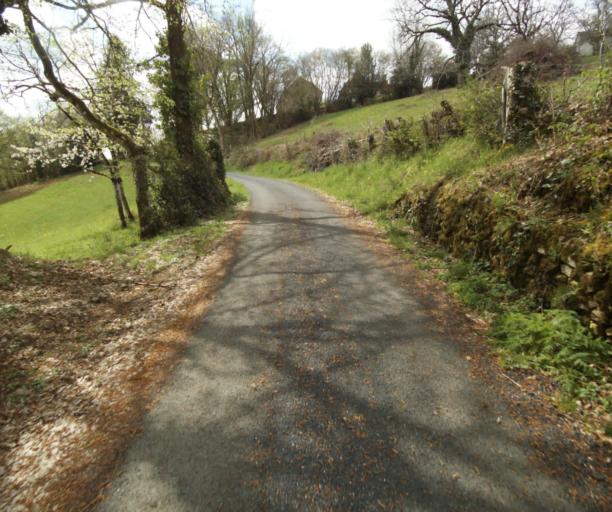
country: FR
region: Limousin
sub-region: Departement de la Correze
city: Sainte-Fortunade
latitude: 45.1899
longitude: 1.8641
